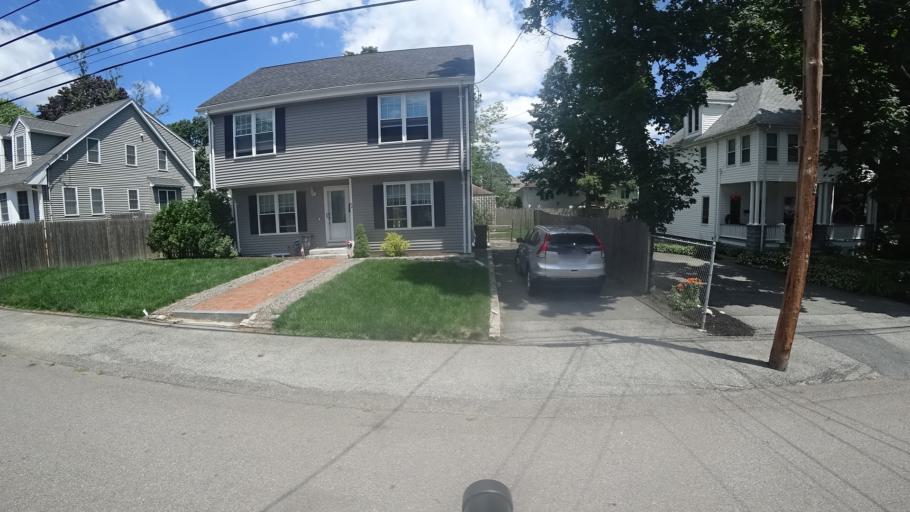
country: US
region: Massachusetts
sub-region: Norfolk County
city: Dedham
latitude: 42.2585
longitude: -71.1768
